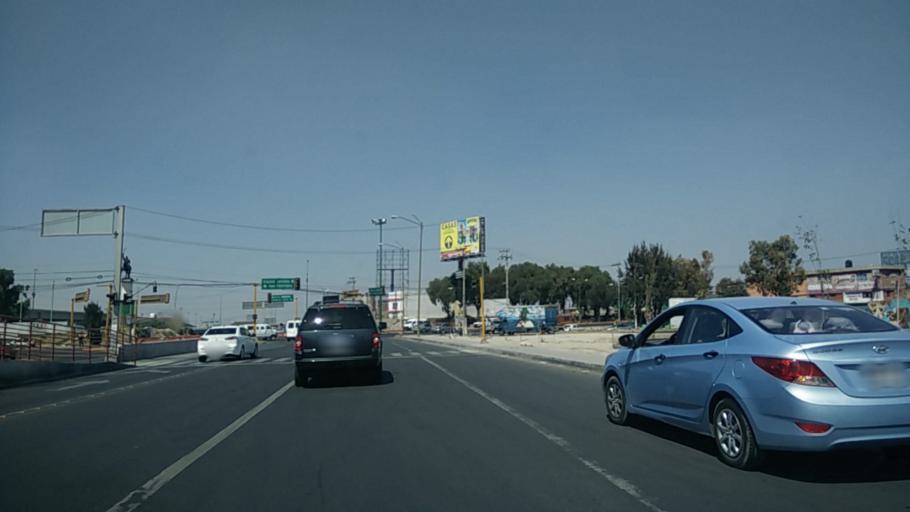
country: MX
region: Mexico
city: Ecatepec
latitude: 19.6011
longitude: -99.0337
